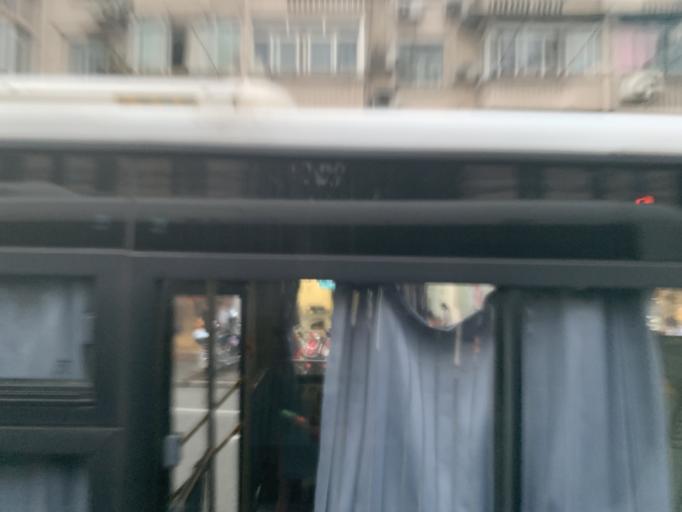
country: CN
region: Shanghai Shi
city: Pudong
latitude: 31.2379
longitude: 121.5186
